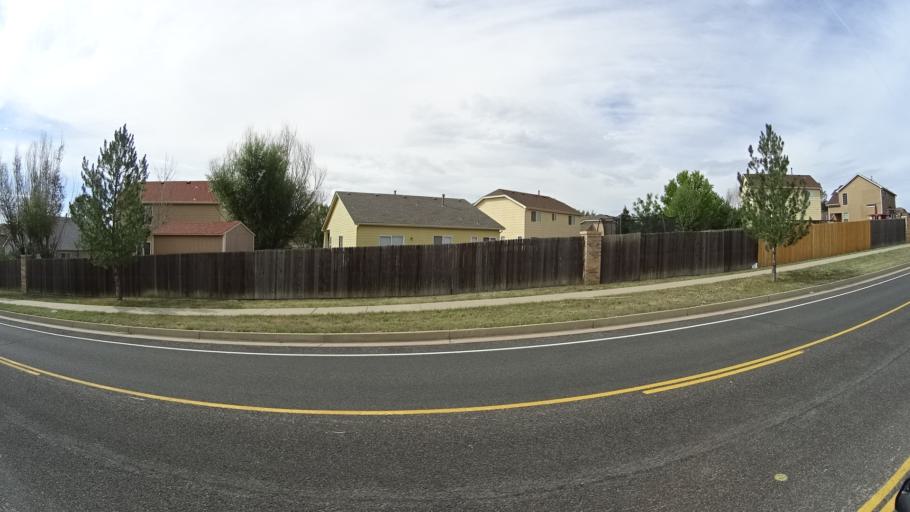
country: US
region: Colorado
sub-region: El Paso County
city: Fountain
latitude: 38.7084
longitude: -104.6890
